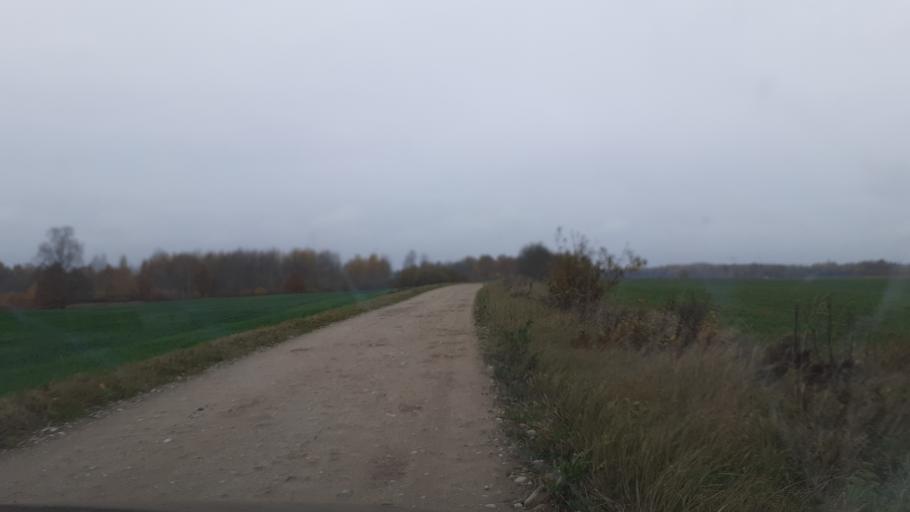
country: LV
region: Saldus Rajons
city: Saldus
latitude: 56.8661
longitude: 22.3453
